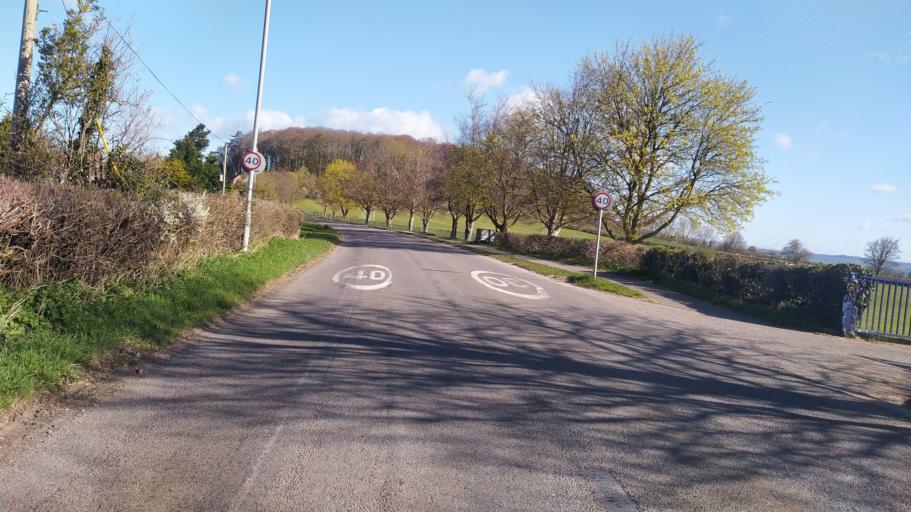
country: GB
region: England
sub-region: Dorset
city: Sturminster Newton
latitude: 50.9350
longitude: -2.3047
